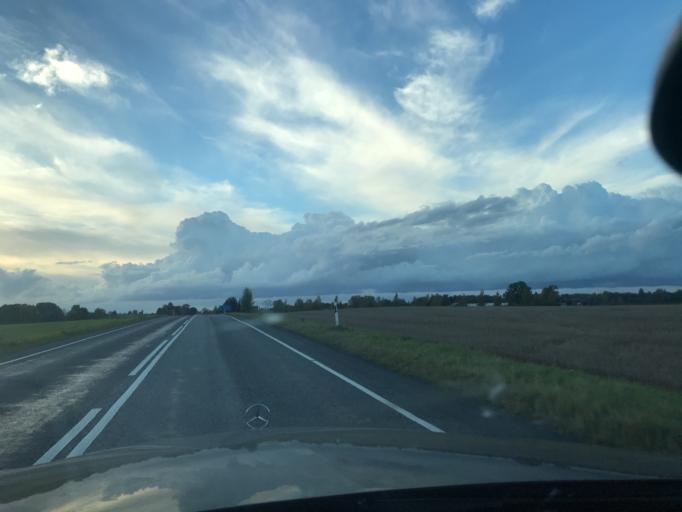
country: EE
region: Vorumaa
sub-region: Antsla vald
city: Vana-Antsla
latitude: 57.8822
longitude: 26.5364
